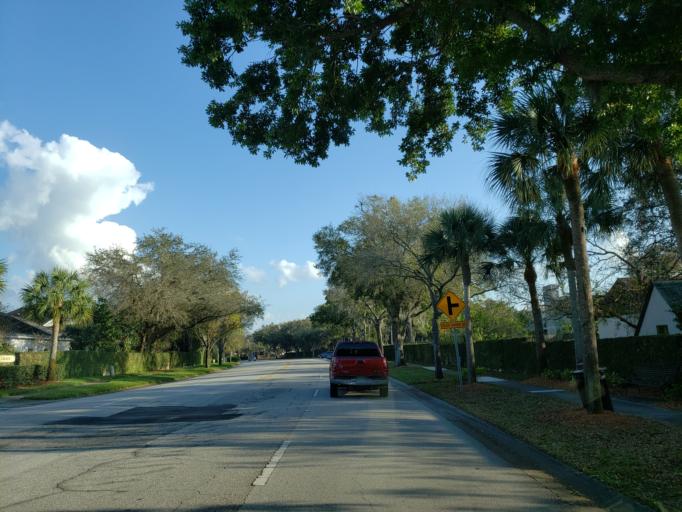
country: US
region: Florida
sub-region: Hillsborough County
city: Bloomingdale
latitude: 27.8779
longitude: -82.2659
